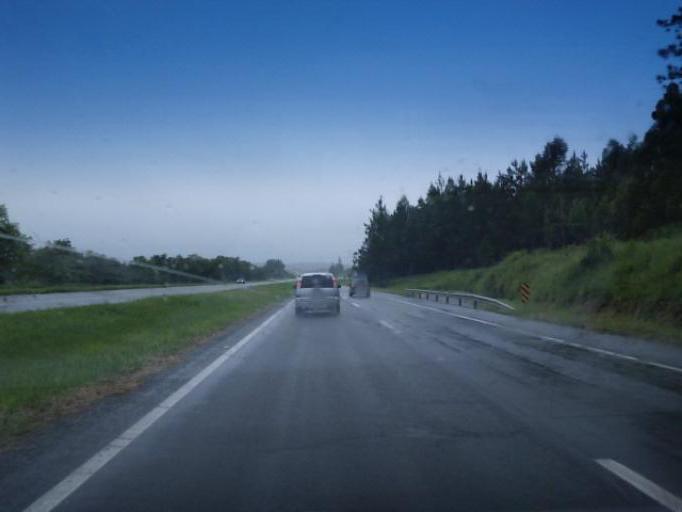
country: BR
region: Sao Paulo
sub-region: Jacupiranga
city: Jacupiranga
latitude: -24.7160
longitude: -48.0338
